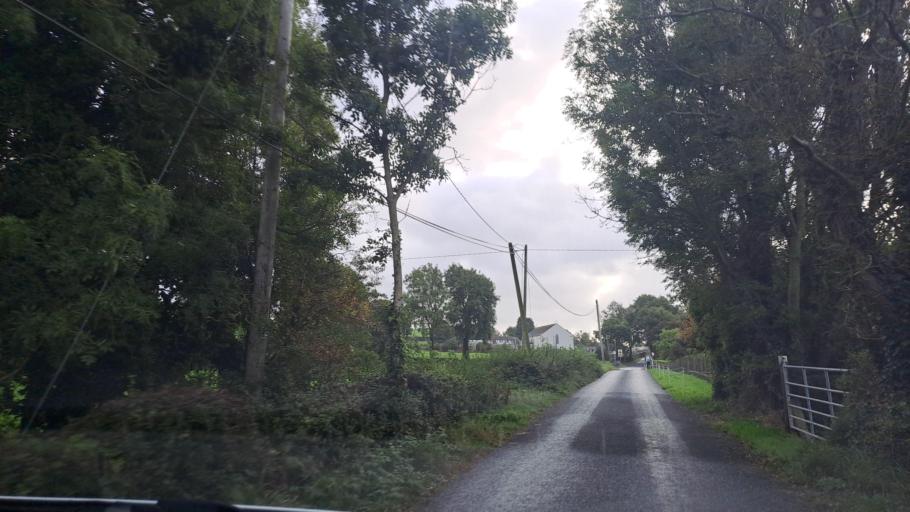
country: IE
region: Ulster
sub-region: An Cabhan
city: Kingscourt
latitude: 53.9534
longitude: -6.7837
